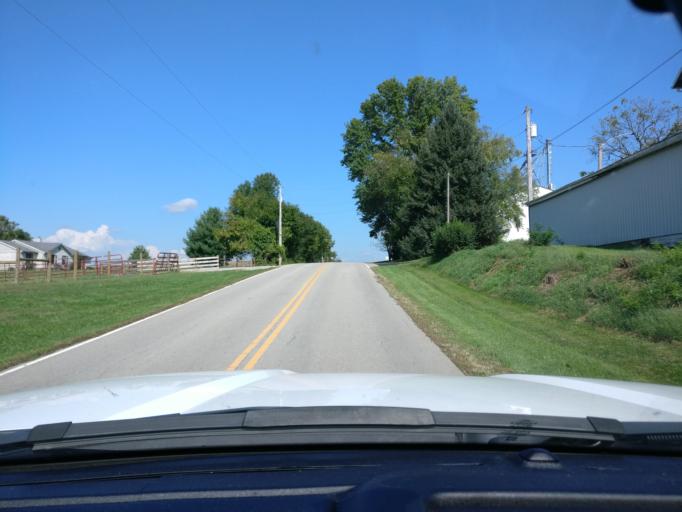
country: US
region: Ohio
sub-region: Warren County
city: Waynesville
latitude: 39.4784
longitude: -83.9931
